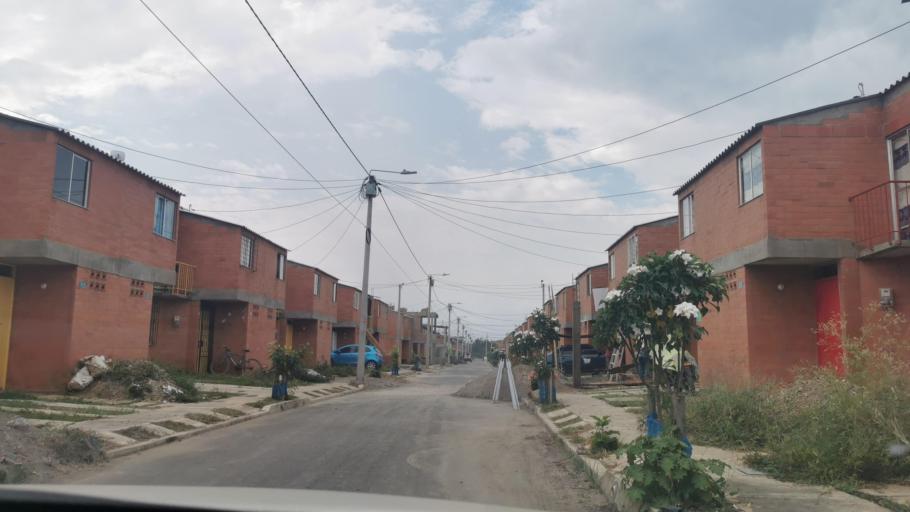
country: CO
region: Valle del Cauca
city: Jamundi
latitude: 3.2338
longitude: -76.5248
